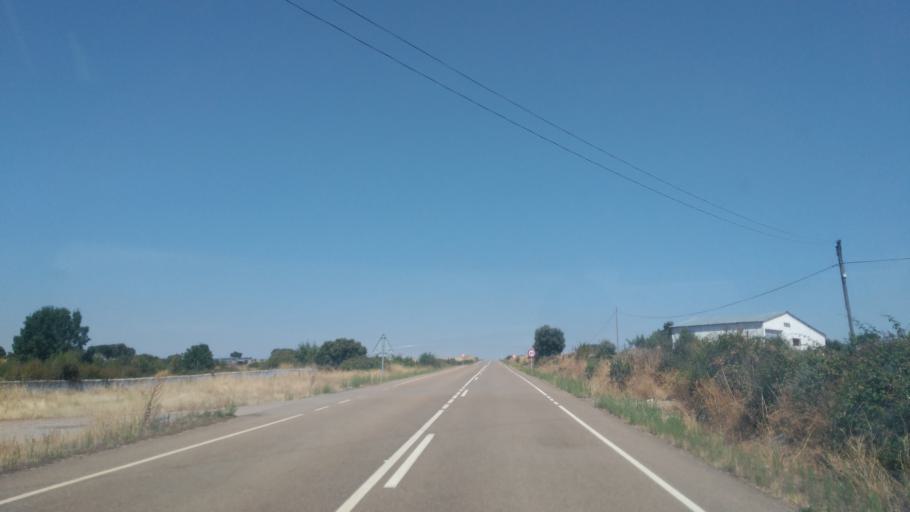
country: ES
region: Castille and Leon
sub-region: Provincia de Salamanca
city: Aldeanueva de la Sierra
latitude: 40.6181
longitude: -6.1013
